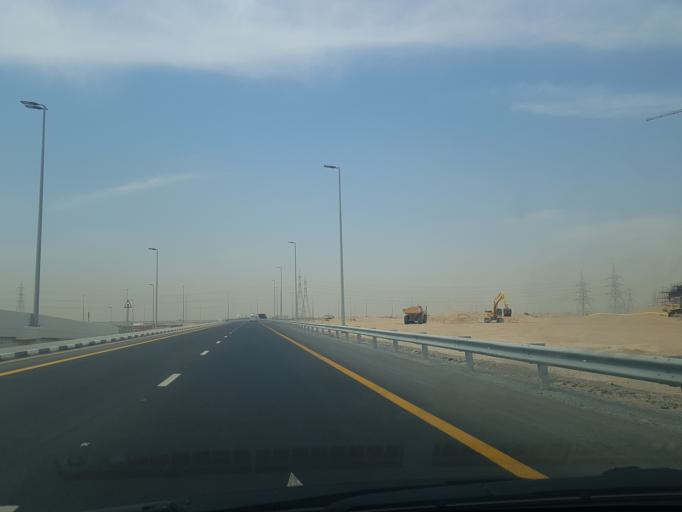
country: AE
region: Ash Shariqah
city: Sharjah
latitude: 25.2392
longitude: 55.5695
